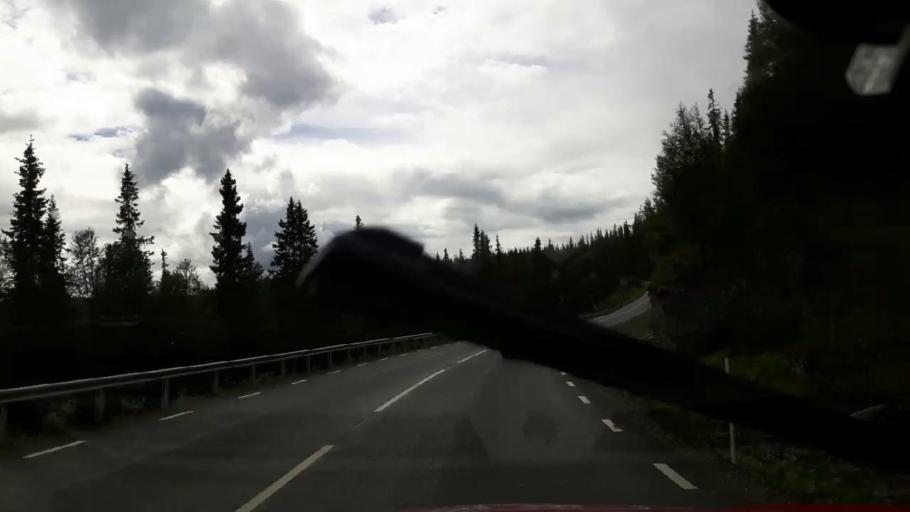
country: NO
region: Nord-Trondelag
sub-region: Royrvik
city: Royrvik
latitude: 64.8558
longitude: 14.1811
